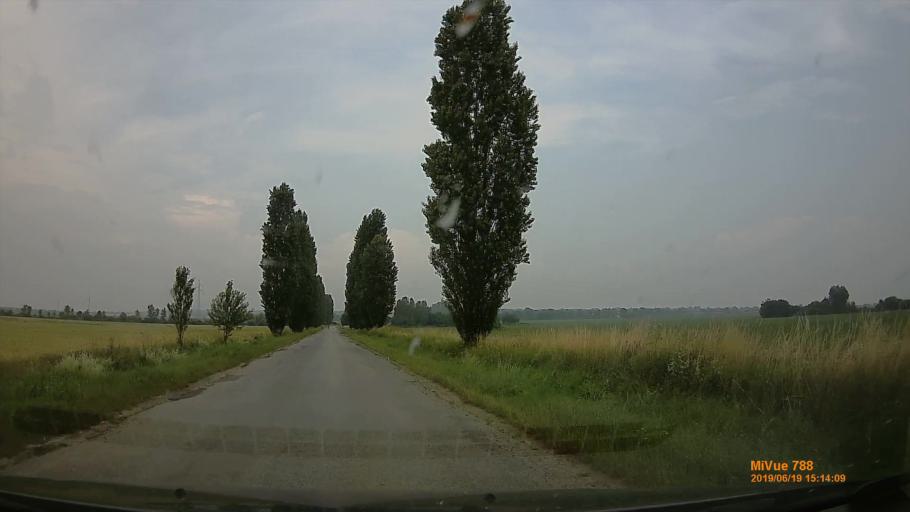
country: HU
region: Baranya
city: Szigetvar
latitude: 46.0662
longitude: 17.8221
